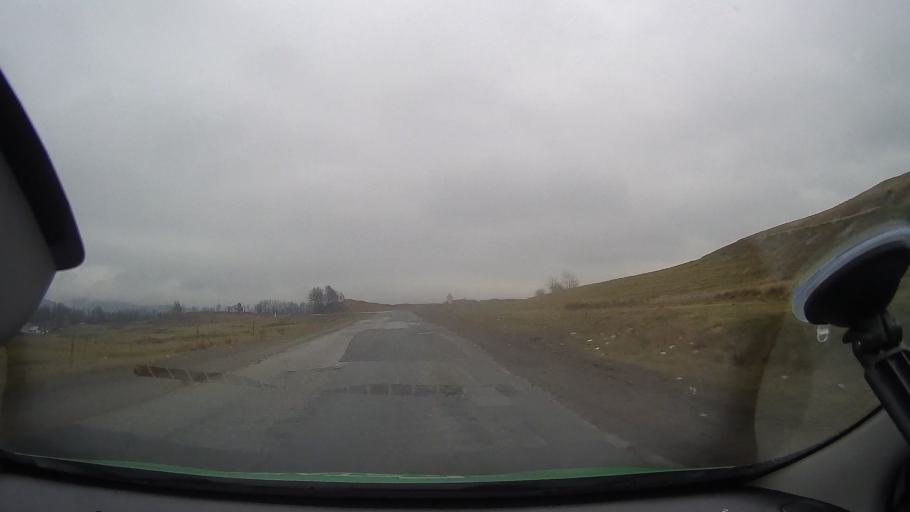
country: RO
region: Arad
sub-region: Comuna Halmagiu
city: Halmagiu
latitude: 46.2819
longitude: 22.5791
